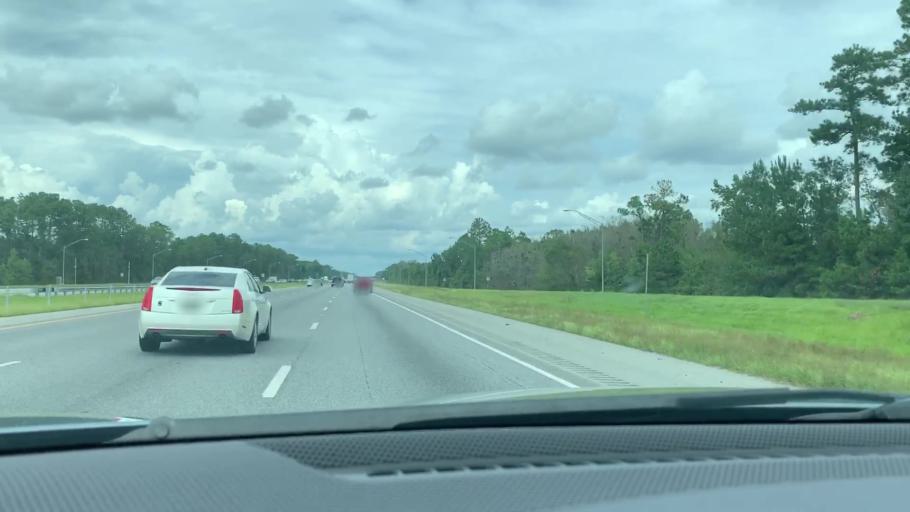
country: US
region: Georgia
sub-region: McIntosh County
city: Darien
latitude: 31.4798
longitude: -81.4471
